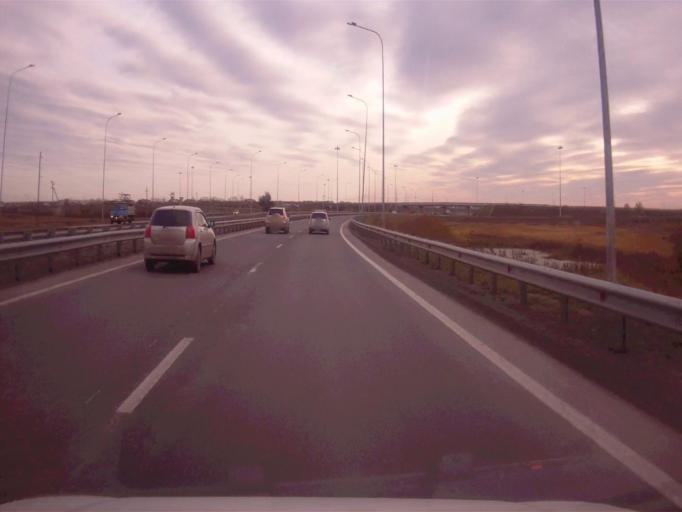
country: RU
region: Chelyabinsk
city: Novosineglazovskiy
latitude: 55.0061
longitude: 61.4534
